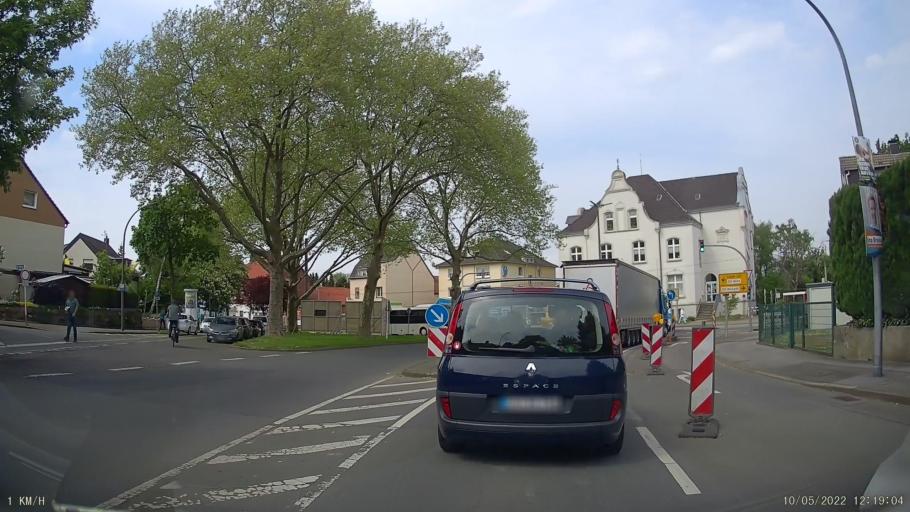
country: DE
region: North Rhine-Westphalia
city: Lanstrop
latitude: 51.5236
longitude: 7.5537
